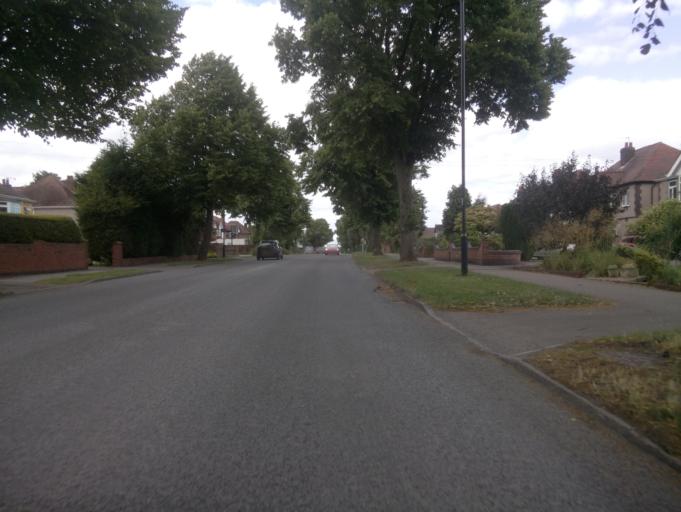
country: GB
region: England
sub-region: Warwickshire
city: Nuneaton
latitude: 52.5348
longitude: -1.4658
